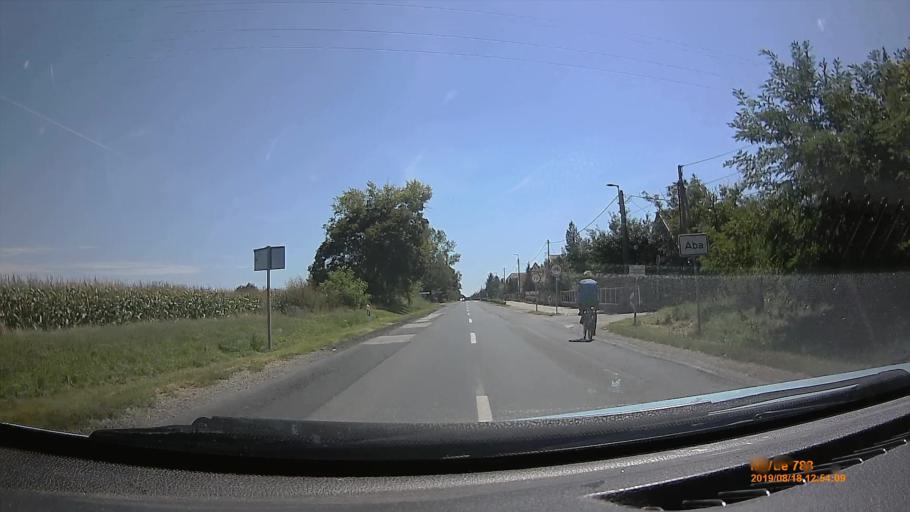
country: HU
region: Fejer
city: Aba
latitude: 47.0439
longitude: 18.5296
